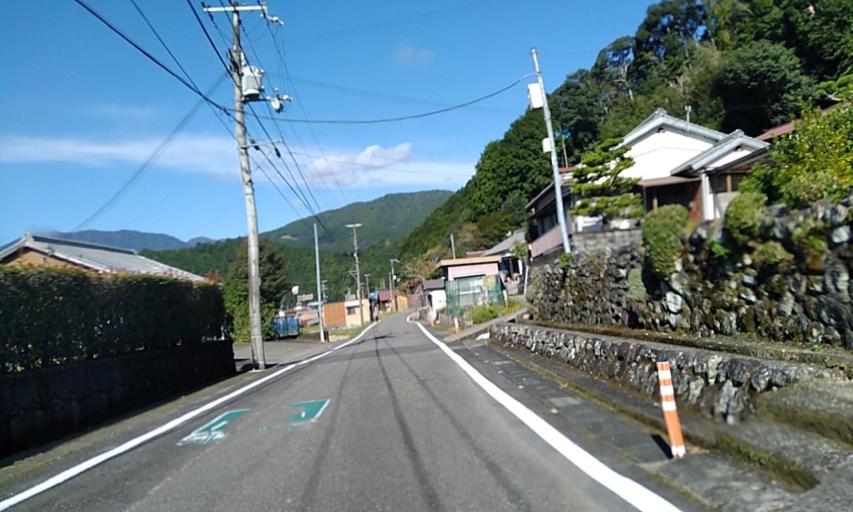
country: JP
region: Wakayama
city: Shingu
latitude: 33.9262
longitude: 135.9822
